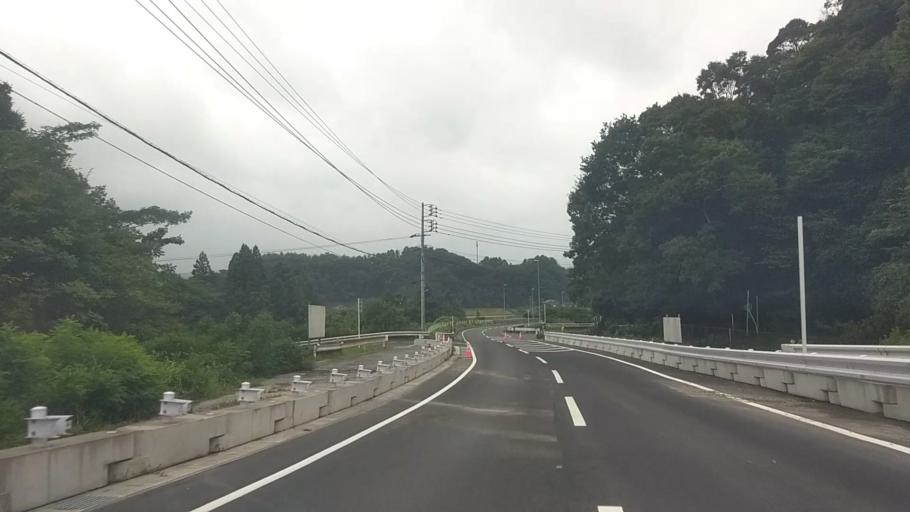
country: JP
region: Chiba
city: Kisarazu
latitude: 35.2610
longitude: 140.0486
